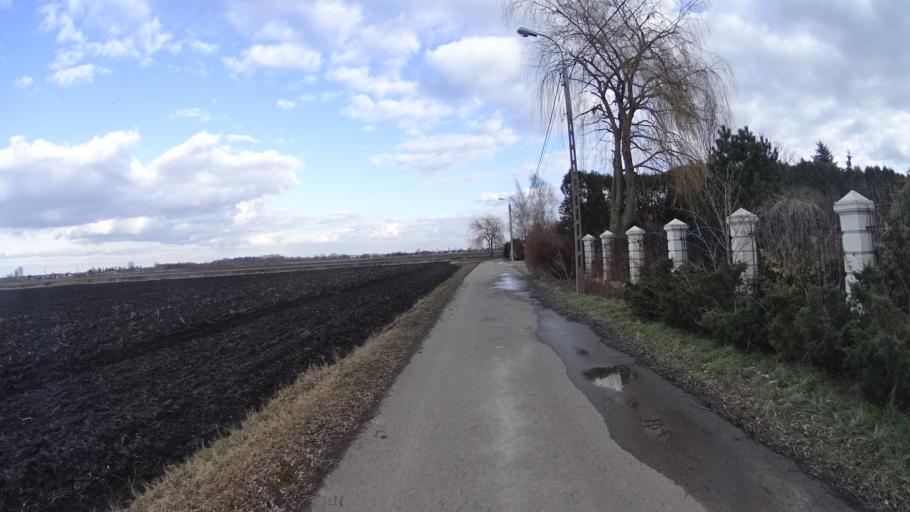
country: PL
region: Masovian Voivodeship
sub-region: Powiat warszawski zachodni
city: Ozarow Mazowiecki
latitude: 52.2464
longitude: 20.7947
